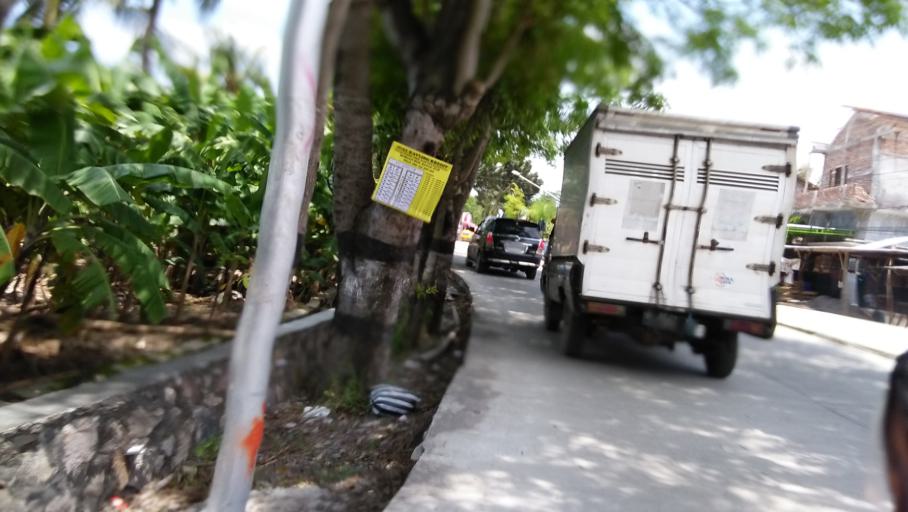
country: ID
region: Central Java
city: Mranggen
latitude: -6.9754
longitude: 110.4814
